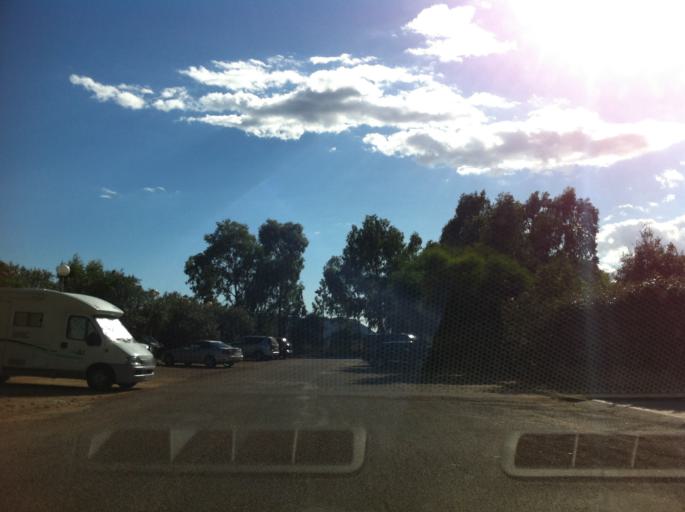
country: FR
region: Corsica
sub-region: Departement de la Corse-du-Sud
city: Porto-Vecchio
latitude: 41.6537
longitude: 9.3236
